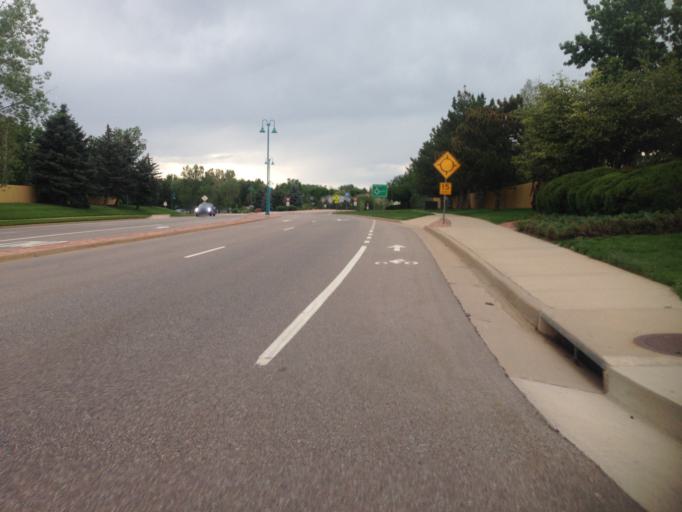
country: US
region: Colorado
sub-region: Boulder County
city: Superior
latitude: 39.9366
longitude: -105.1465
